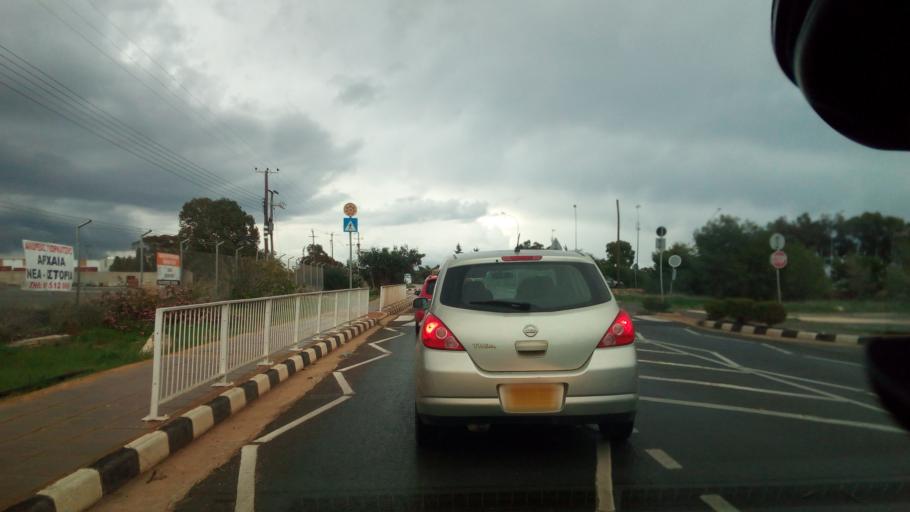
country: CY
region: Ammochostos
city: Frenaros
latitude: 35.0309
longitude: 33.9141
